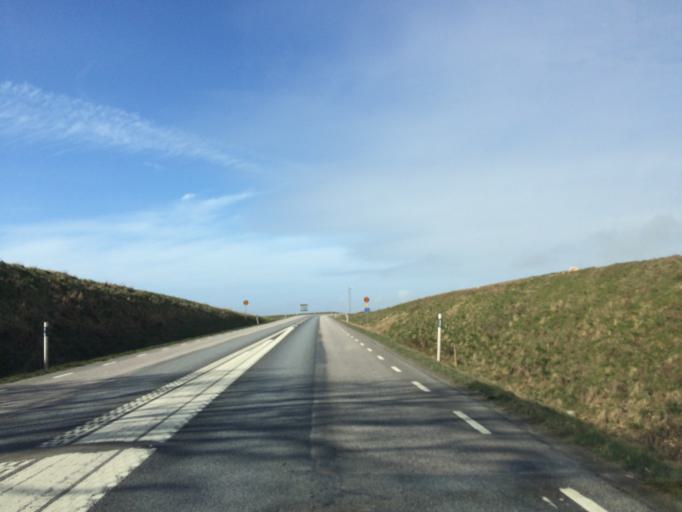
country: SE
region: Halland
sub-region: Halmstads Kommun
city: Paarp
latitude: 56.5890
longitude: 12.9864
